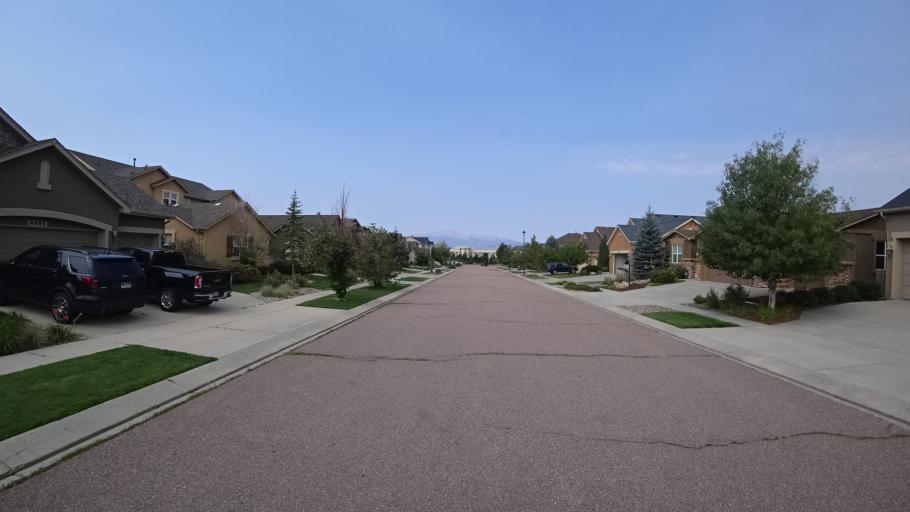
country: US
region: Colorado
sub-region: El Paso County
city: Black Forest
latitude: 38.9682
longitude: -104.7350
